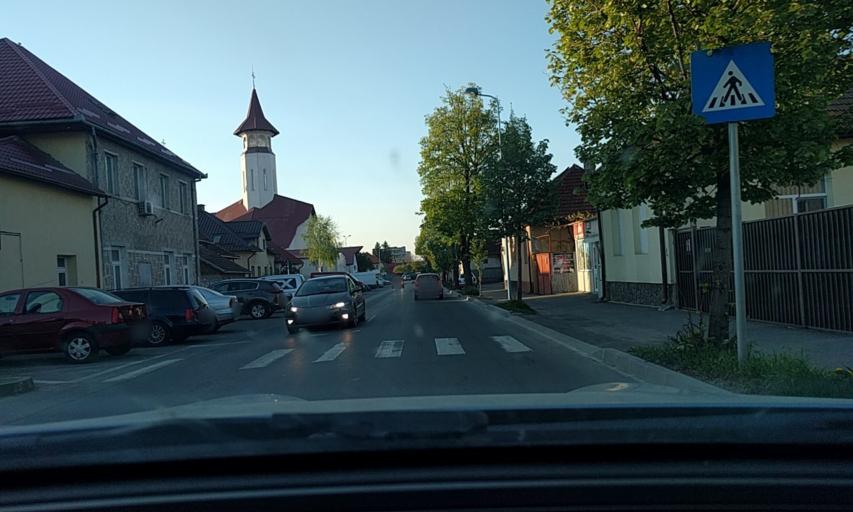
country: RO
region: Brasov
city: Brasov
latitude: 45.6651
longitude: 25.5780
